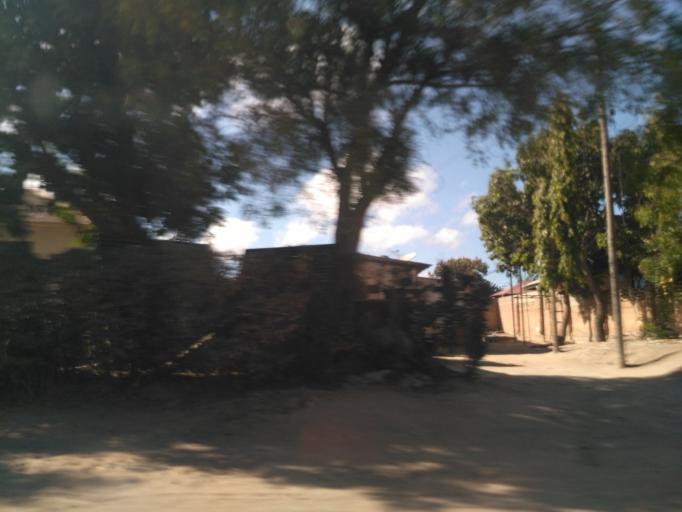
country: TZ
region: Dodoma
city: Dodoma
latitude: -6.1851
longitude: 35.7405
